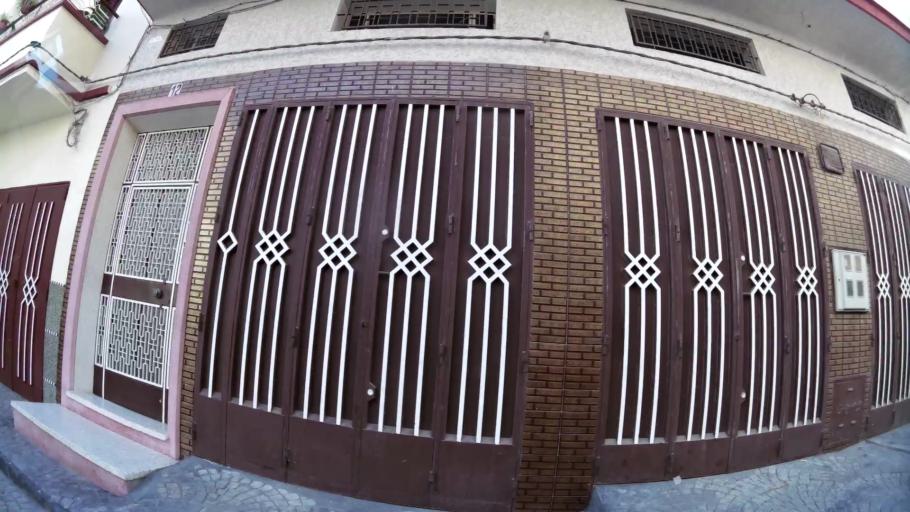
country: MA
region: Tanger-Tetouan
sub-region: Tanger-Assilah
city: Tangier
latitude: 35.7596
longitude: -5.8051
